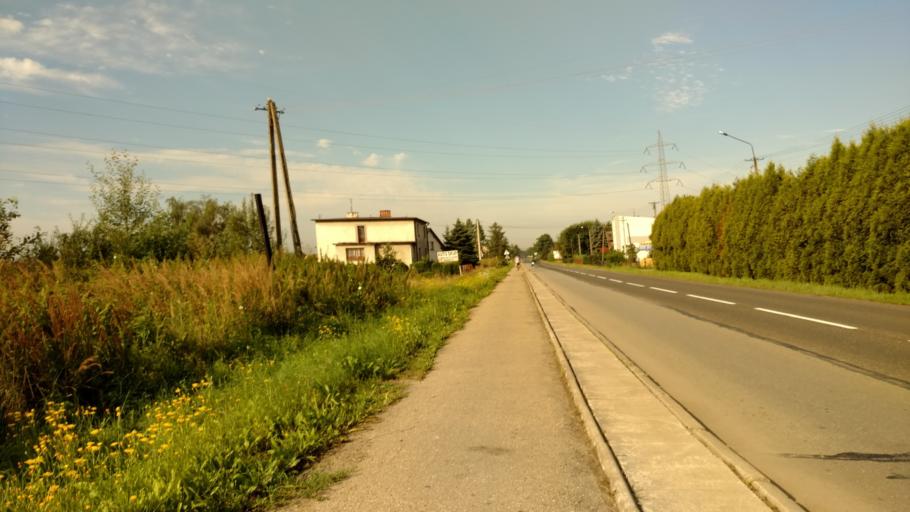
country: PL
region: Silesian Voivodeship
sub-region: Powiat pszczynski
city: Jankowice
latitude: 49.9965
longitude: 18.9724
